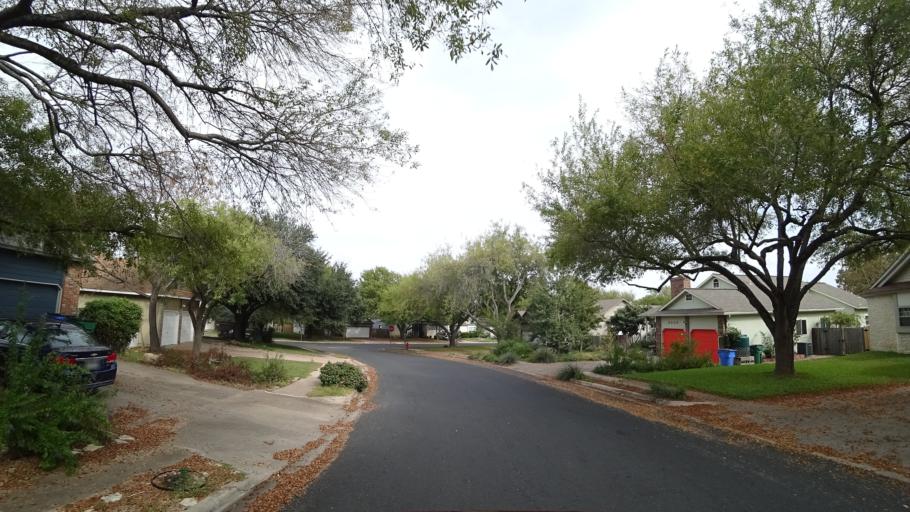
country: US
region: Texas
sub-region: Travis County
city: Wells Branch
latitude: 30.4447
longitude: -97.6816
